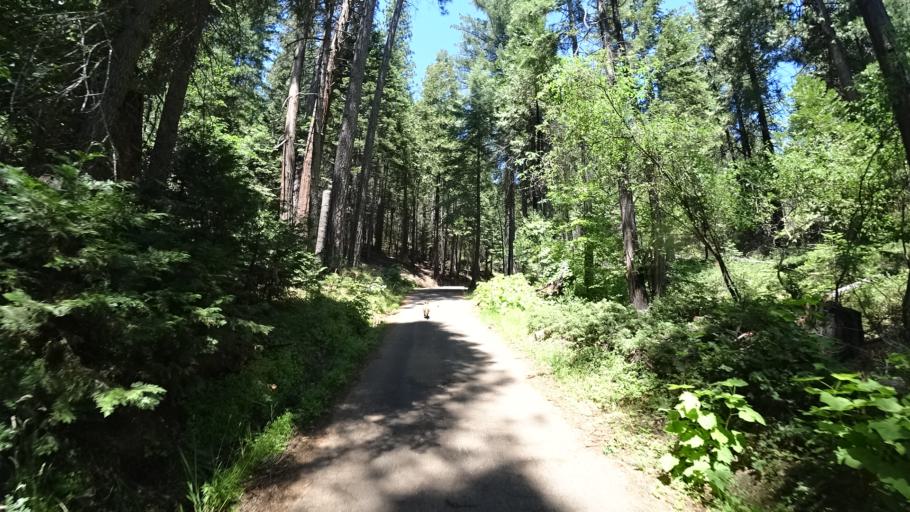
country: US
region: California
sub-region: Calaveras County
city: Arnold
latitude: 38.2517
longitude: -120.3063
